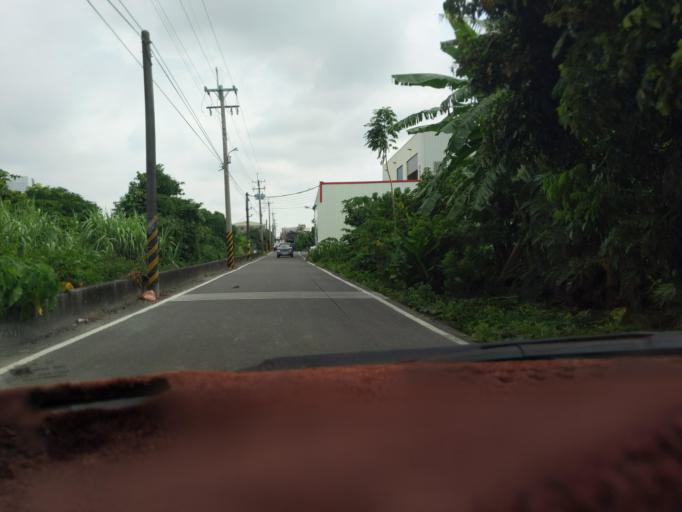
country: TW
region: Taiwan
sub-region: Yunlin
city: Douliu
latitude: 23.8020
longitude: 120.4472
